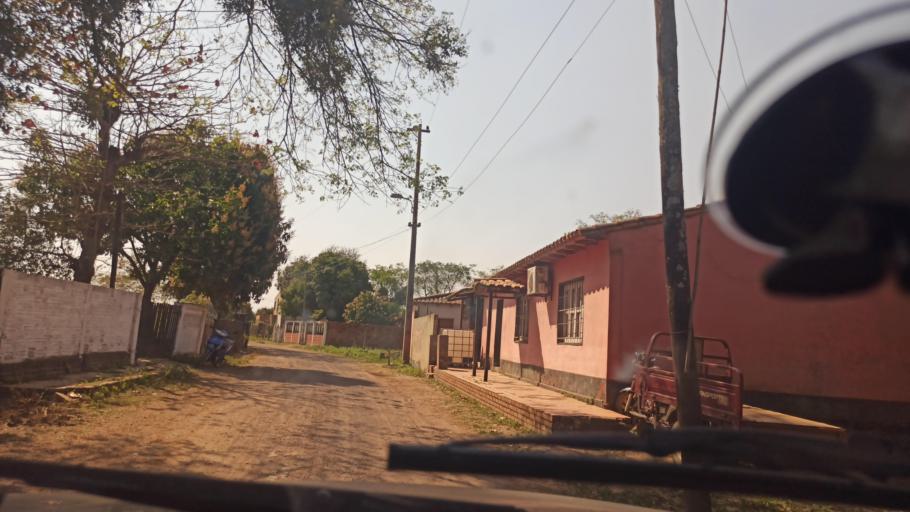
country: AR
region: Formosa
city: Clorinda
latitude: -25.3124
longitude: -57.6978
